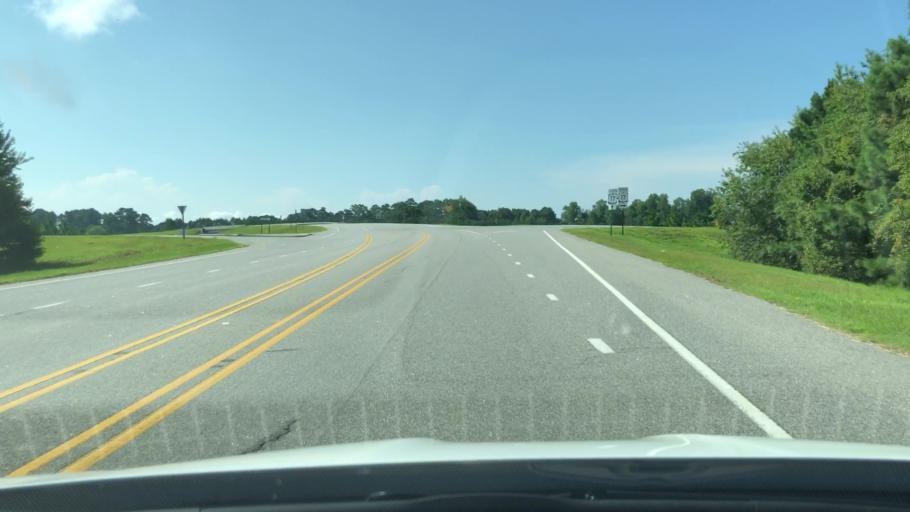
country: US
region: North Carolina
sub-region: Chowan County
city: Edenton
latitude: 36.0622
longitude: -76.6699
